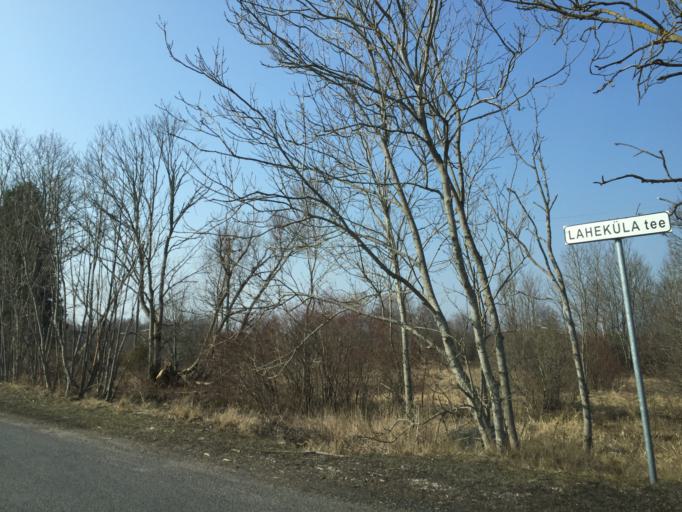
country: EE
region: Saare
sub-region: Kuressaare linn
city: Kuressaare
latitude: 58.2728
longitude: 22.4567
